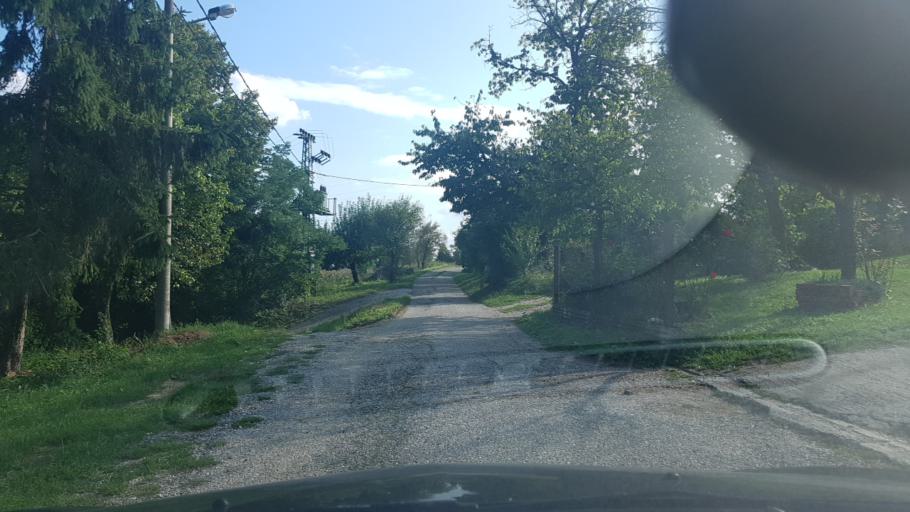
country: HR
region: Krapinsko-Zagorska
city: Radoboj
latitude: 46.1543
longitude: 15.9354
